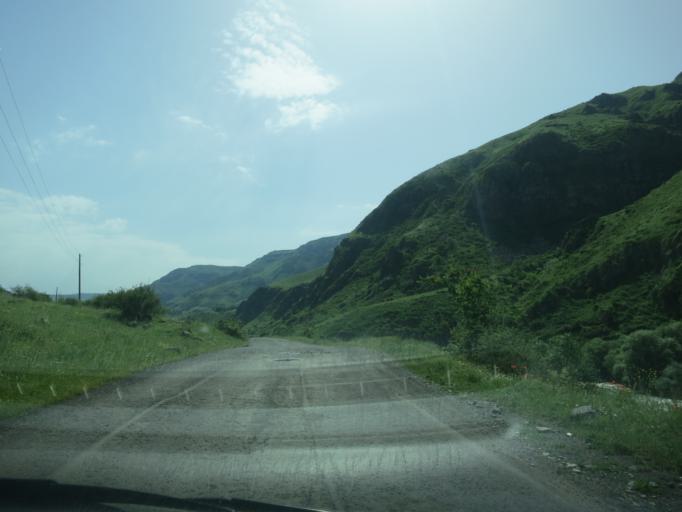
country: TR
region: Ardahan
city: Kurtkale
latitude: 41.3733
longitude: 43.2647
